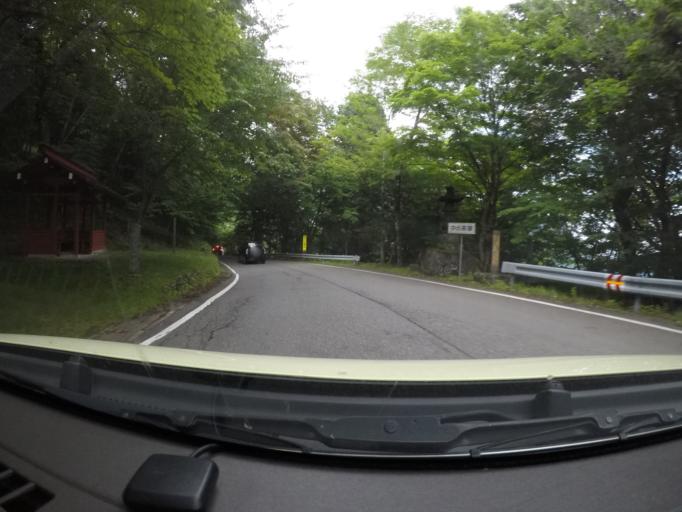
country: JP
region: Tochigi
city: Nikko
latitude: 36.7451
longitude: 139.5126
